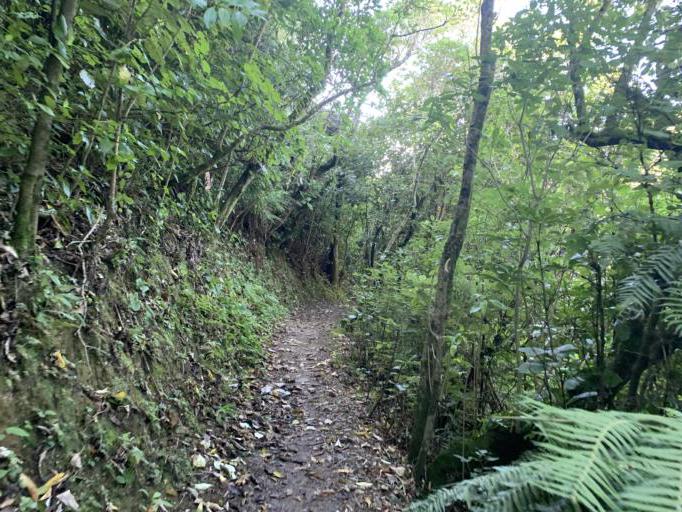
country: NZ
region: Wellington
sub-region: Wellington City
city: Kelburn
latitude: -41.2979
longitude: 174.7545
